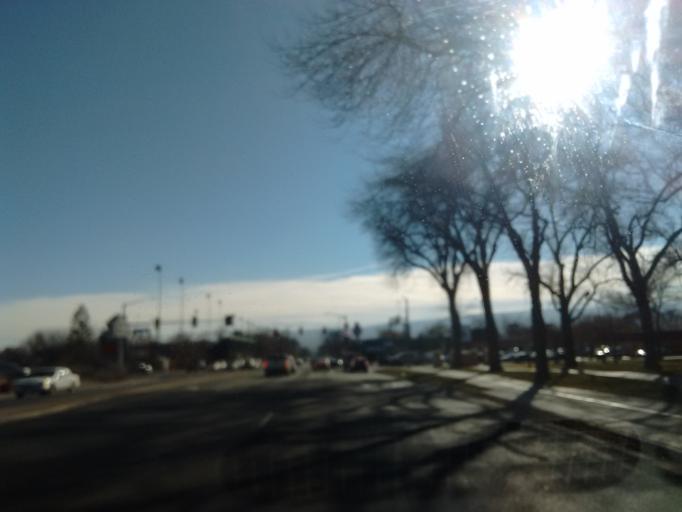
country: US
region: Colorado
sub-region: Mesa County
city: Grand Junction
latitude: 39.0781
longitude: -108.5525
